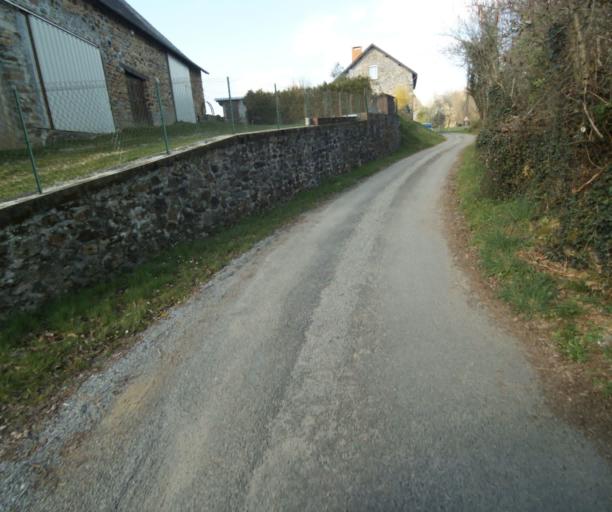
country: FR
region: Limousin
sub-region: Departement de la Correze
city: Saint-Mexant
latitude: 45.3383
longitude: 1.5943
